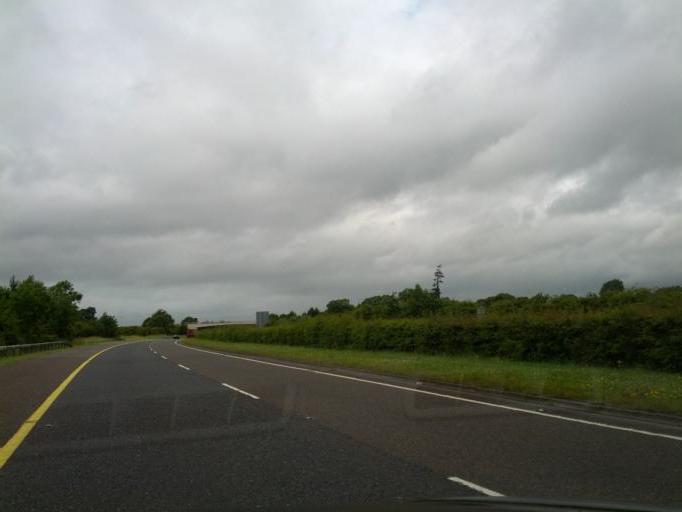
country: IE
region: Munster
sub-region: An Clar
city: Newmarket on Fergus
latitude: 52.7564
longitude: -8.9122
